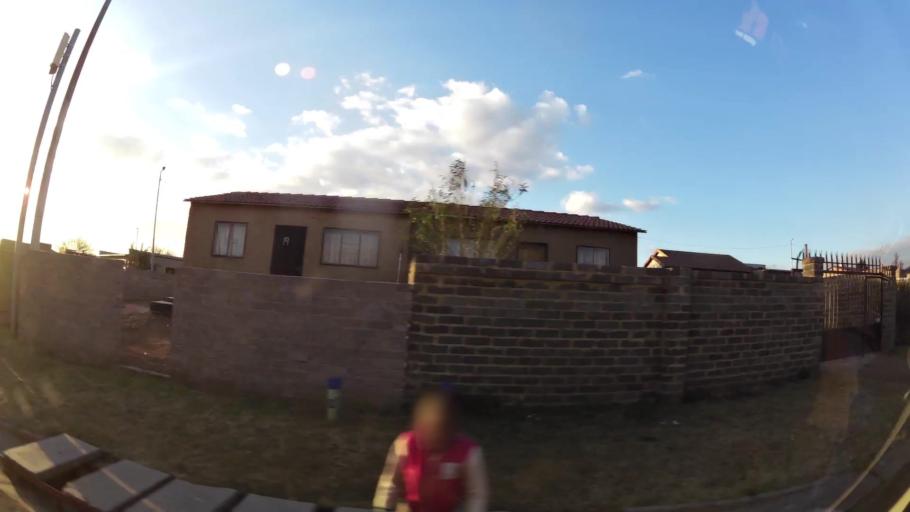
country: ZA
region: Gauteng
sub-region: West Rand District Municipality
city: Krugersdorp
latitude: -26.0749
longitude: 27.7563
